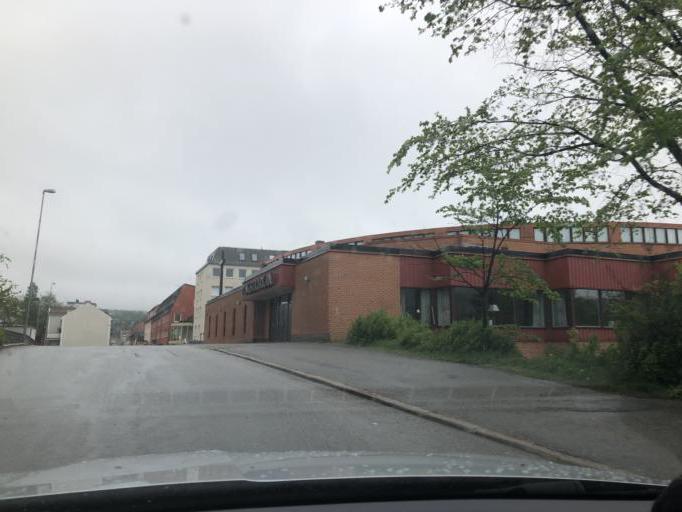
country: SE
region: Vaesternorrland
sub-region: OErnskoeldsviks Kommun
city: Ornskoldsvik
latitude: 63.2898
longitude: 18.7116
